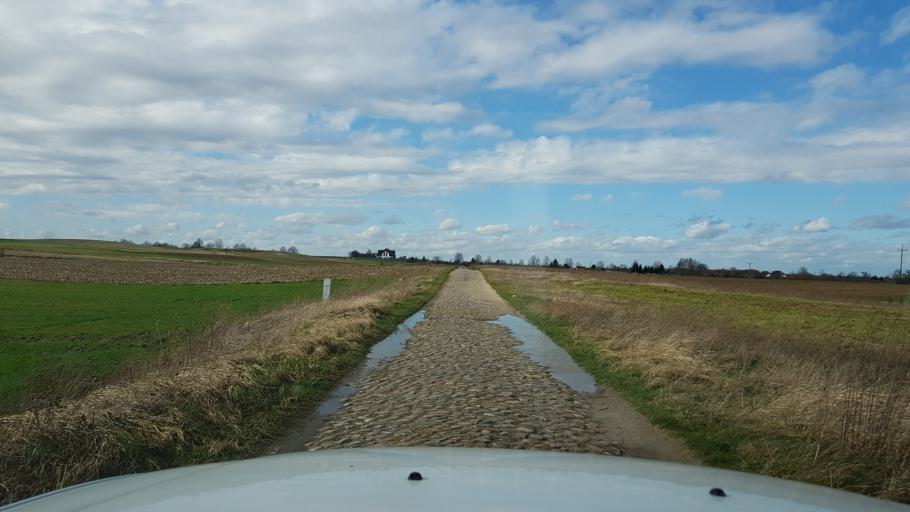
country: PL
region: West Pomeranian Voivodeship
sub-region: Powiat mysliborski
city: Barlinek
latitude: 52.9741
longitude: 15.1810
